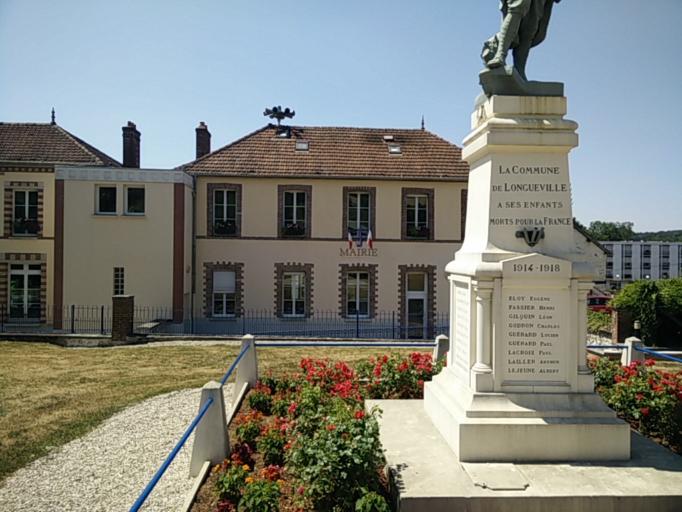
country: FR
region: Ile-de-France
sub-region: Departement de Seine-et-Marne
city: Longueville
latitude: 48.5148
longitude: 3.2478
